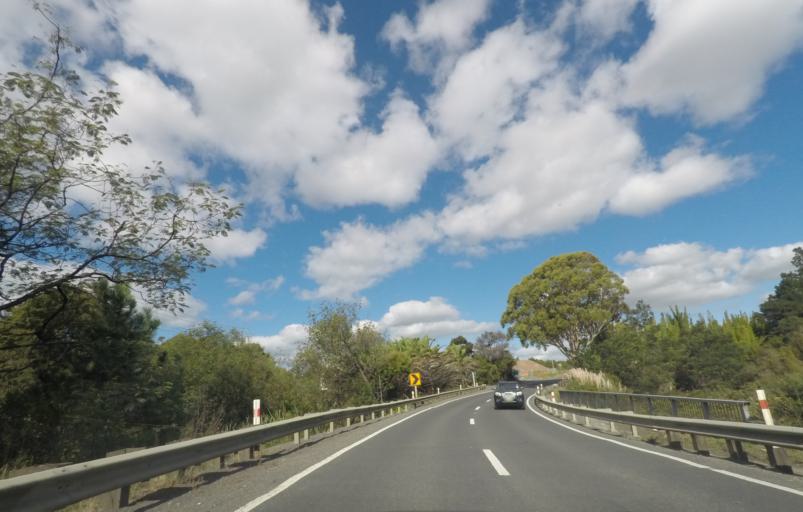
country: NZ
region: Auckland
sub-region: Auckland
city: Rothesay Bay
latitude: -36.5991
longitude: 174.6602
